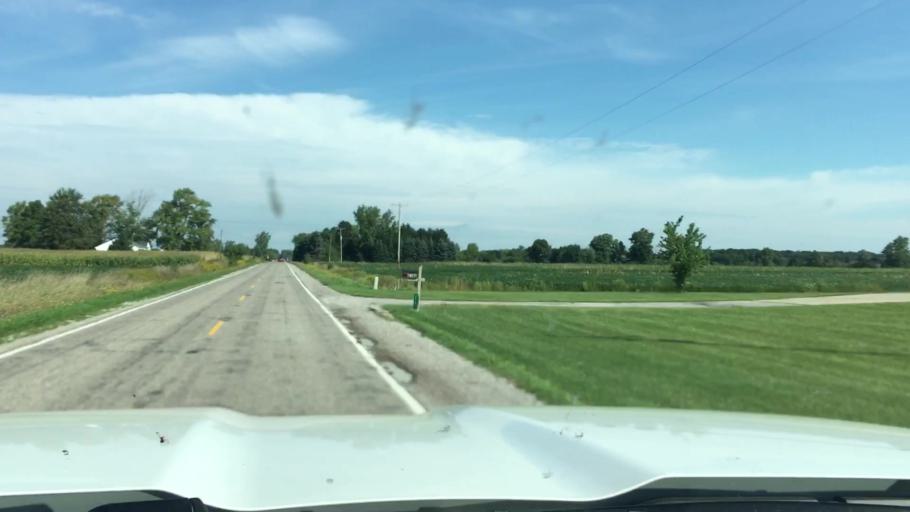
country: US
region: Michigan
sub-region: Saginaw County
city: Hemlock
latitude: 43.4388
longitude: -84.2300
